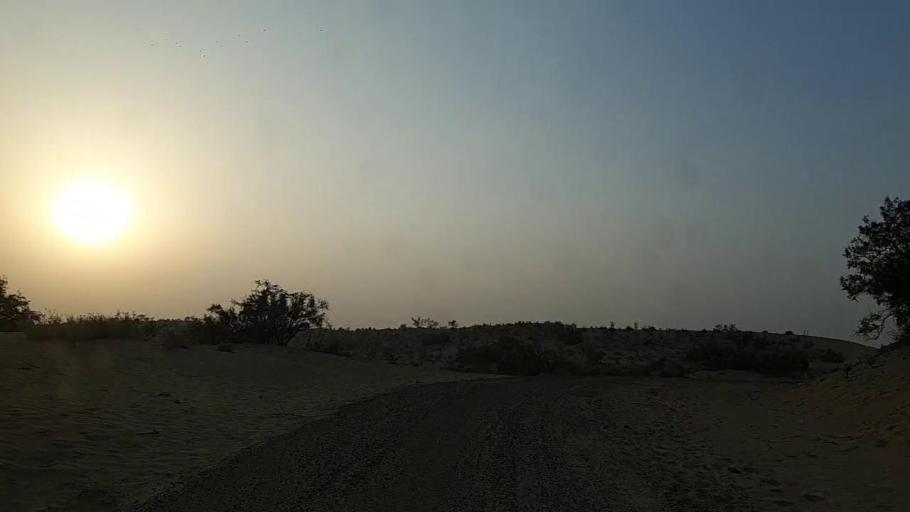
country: PK
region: Sindh
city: Naukot
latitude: 24.6813
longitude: 69.4567
